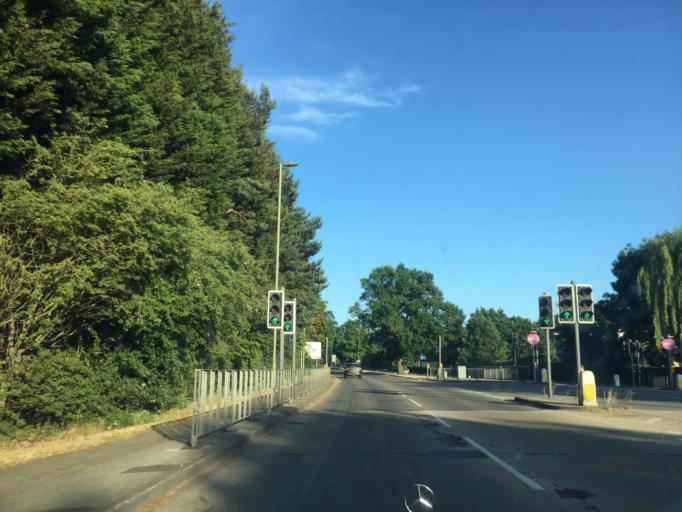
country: GB
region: England
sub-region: Surrey
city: Frimley
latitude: 51.3174
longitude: -0.7477
